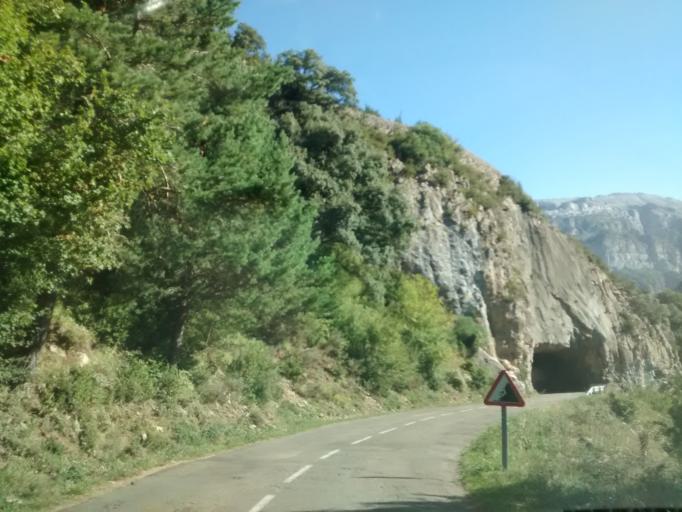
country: ES
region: Aragon
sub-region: Provincia de Huesca
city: Anso
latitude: 42.7859
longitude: -0.7377
